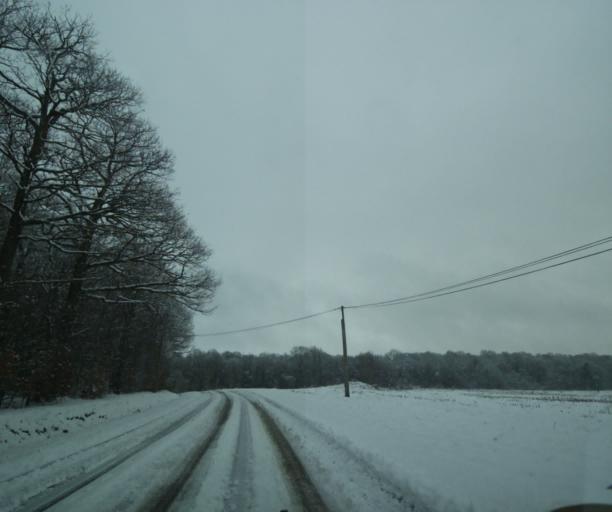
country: FR
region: Champagne-Ardenne
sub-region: Departement de la Haute-Marne
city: Montier-en-Der
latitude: 48.5448
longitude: 4.8001
